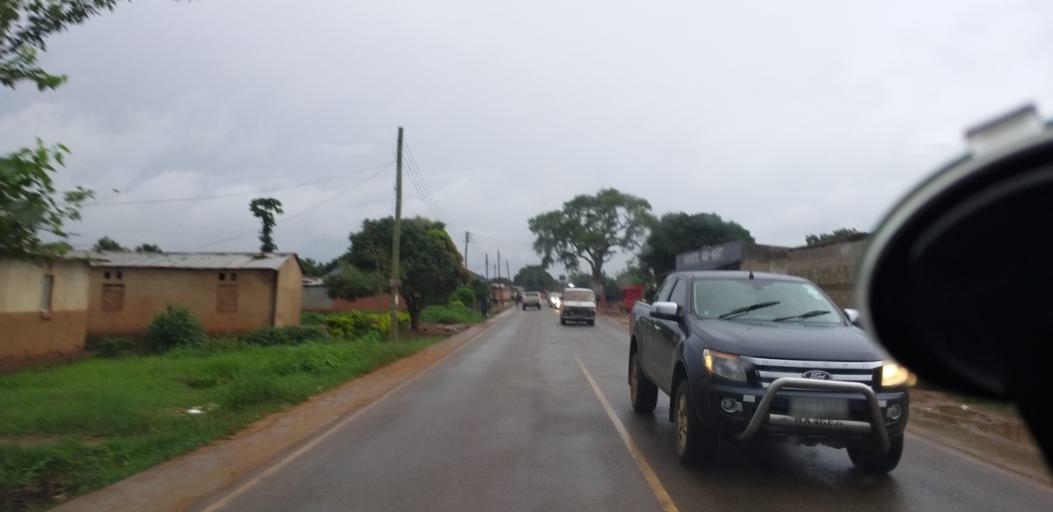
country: ZM
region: Lusaka
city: Lusaka
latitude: -15.5150
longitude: 28.2981
